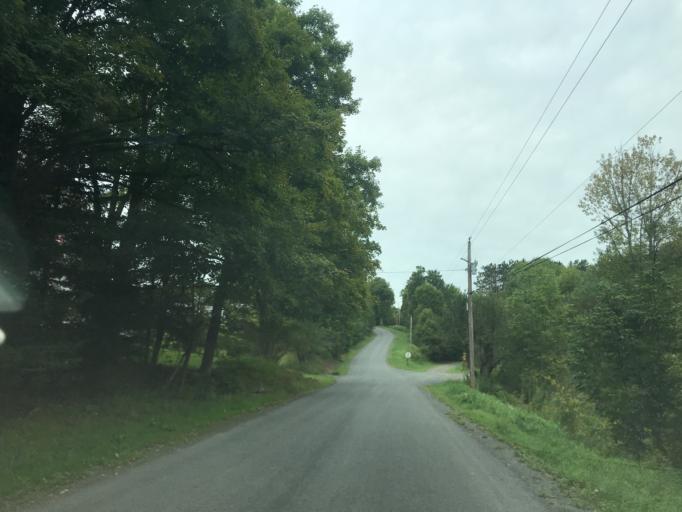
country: US
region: New York
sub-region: Otsego County
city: Worcester
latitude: 42.5210
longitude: -74.6649
